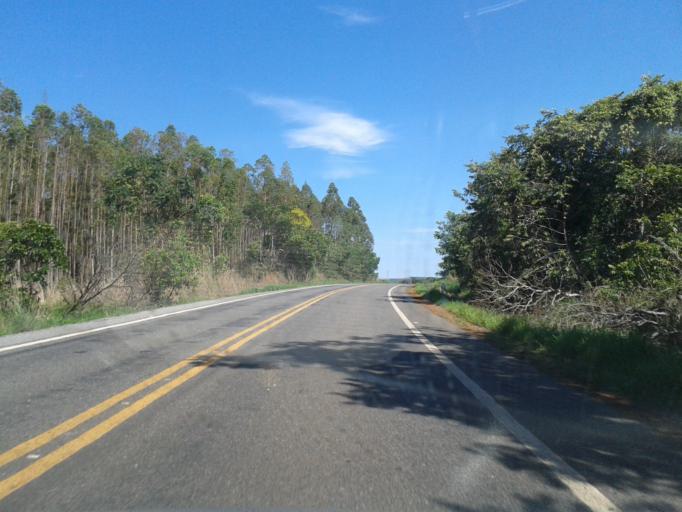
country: BR
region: Goias
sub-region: Piracanjuba
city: Piracanjuba
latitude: -17.3278
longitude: -48.8010
